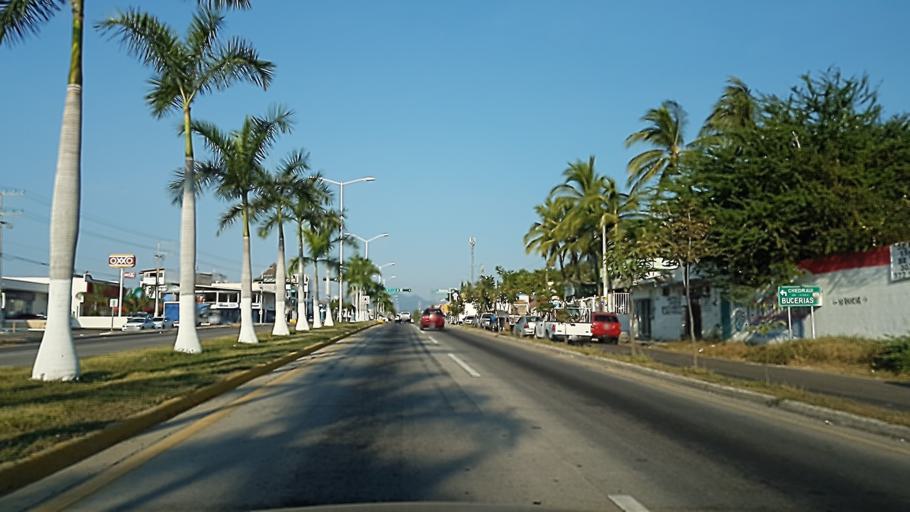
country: MX
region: Nayarit
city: Bucerias
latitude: 20.7513
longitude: -105.3246
